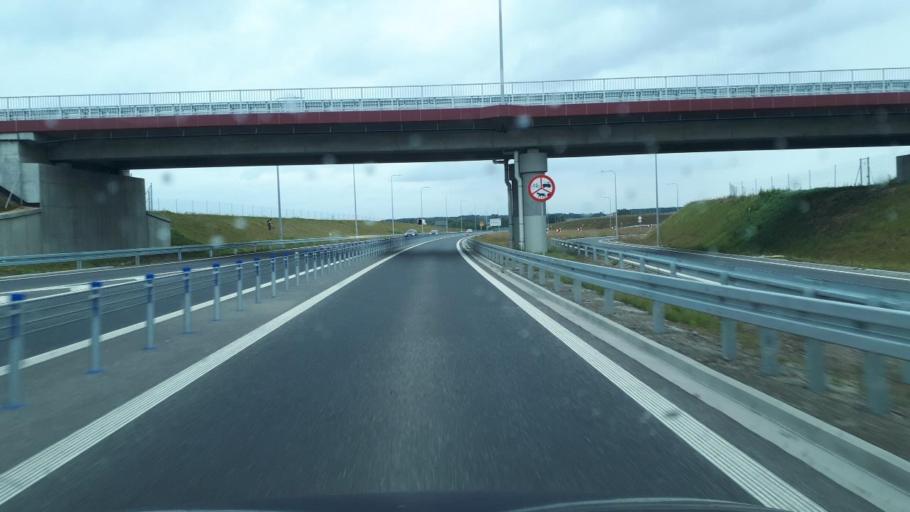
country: PL
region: Greater Poland Voivodeship
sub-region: Powiat kepinski
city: Baranow
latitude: 51.2556
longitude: 18.0154
